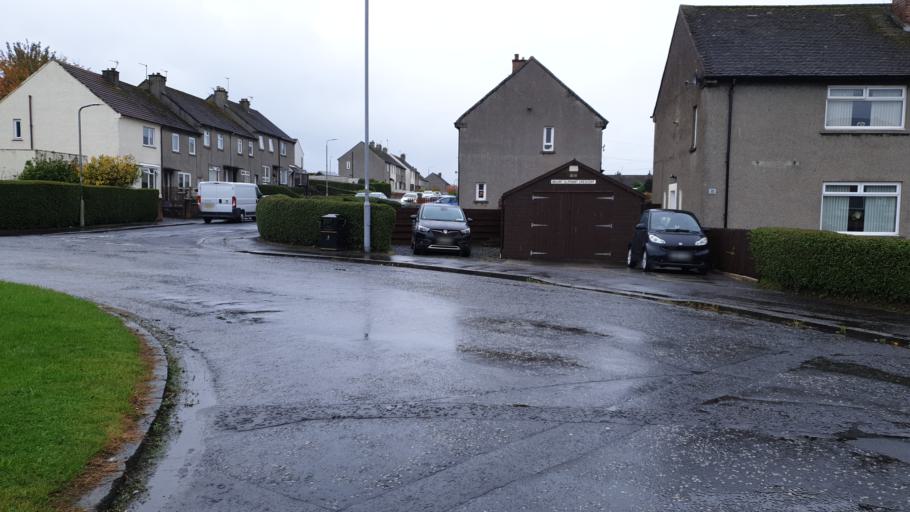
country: GB
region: Scotland
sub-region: South Ayrshire
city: Ayr
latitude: 55.4512
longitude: -4.6138
